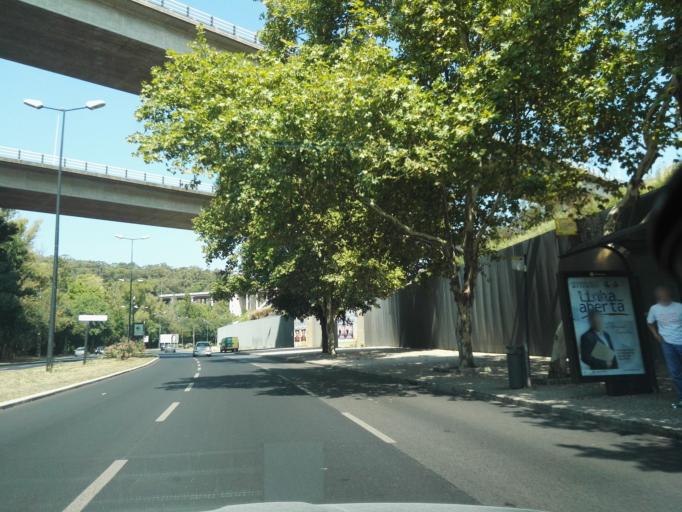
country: PT
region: Lisbon
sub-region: Lisbon
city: Lisbon
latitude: 38.7192
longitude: -9.1748
